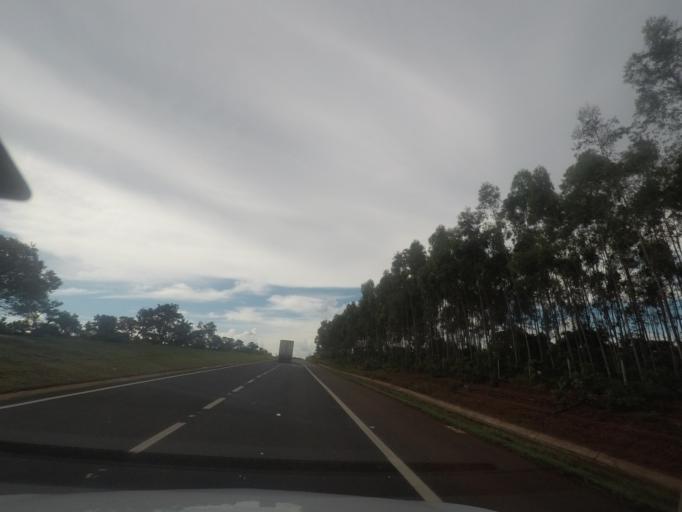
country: BR
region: Minas Gerais
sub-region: Prata
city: Prata
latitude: -19.3992
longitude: -48.8959
